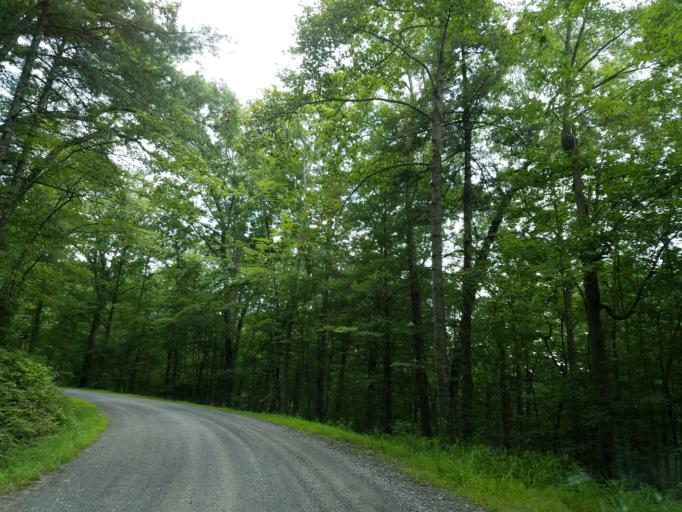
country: US
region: Georgia
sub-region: Fannin County
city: Blue Ridge
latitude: 34.8161
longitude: -84.2425
